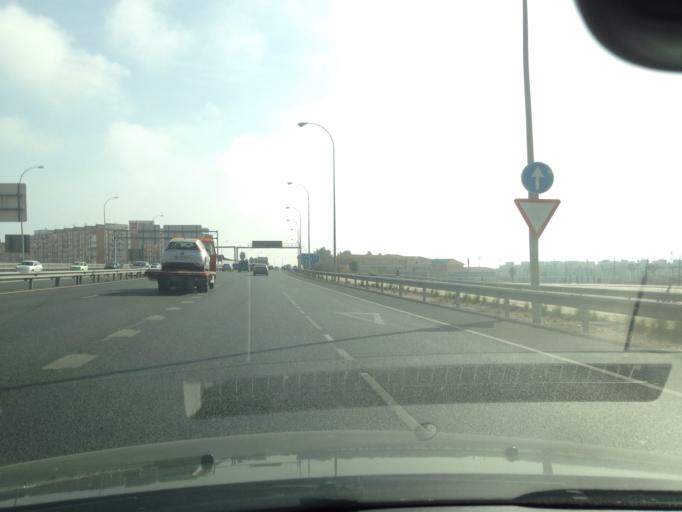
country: ES
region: Andalusia
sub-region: Provincia de Malaga
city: Malaga
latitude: 36.7018
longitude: -4.4580
